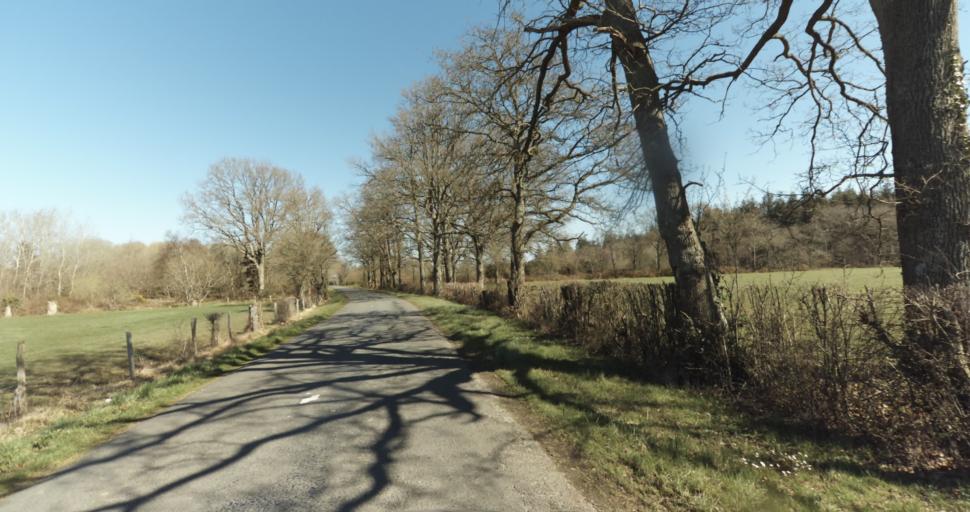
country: FR
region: Lower Normandy
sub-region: Departement du Calvados
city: Livarot
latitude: 48.9496
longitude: 0.0886
